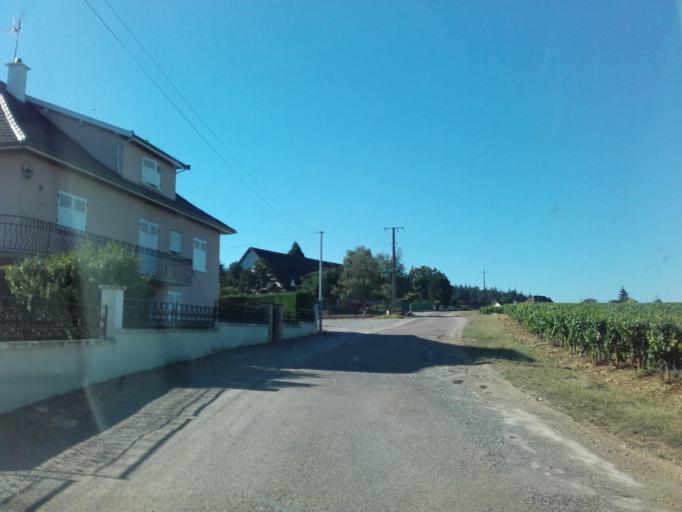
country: FR
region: Bourgogne
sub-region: Departement de Saone-et-Loire
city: Mellecey
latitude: 46.8359
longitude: 4.7355
